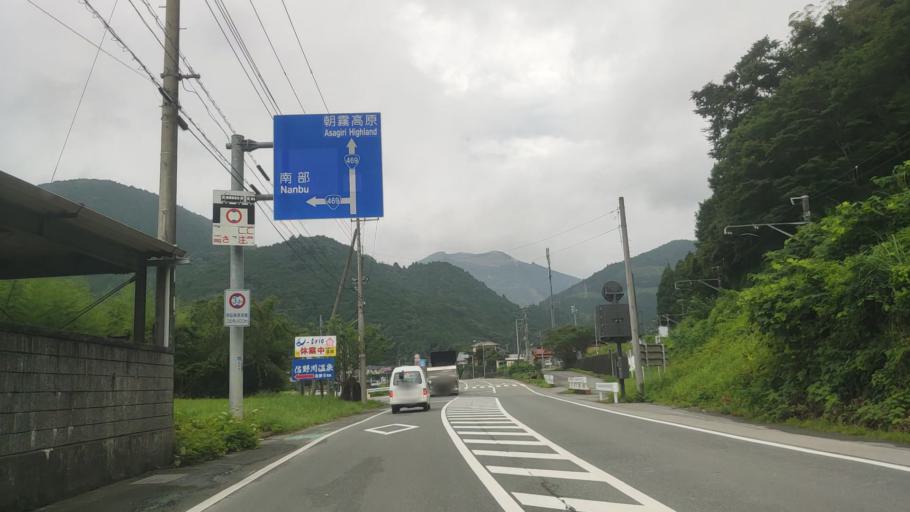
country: JP
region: Shizuoka
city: Fujinomiya
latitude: 35.2293
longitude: 138.5372
